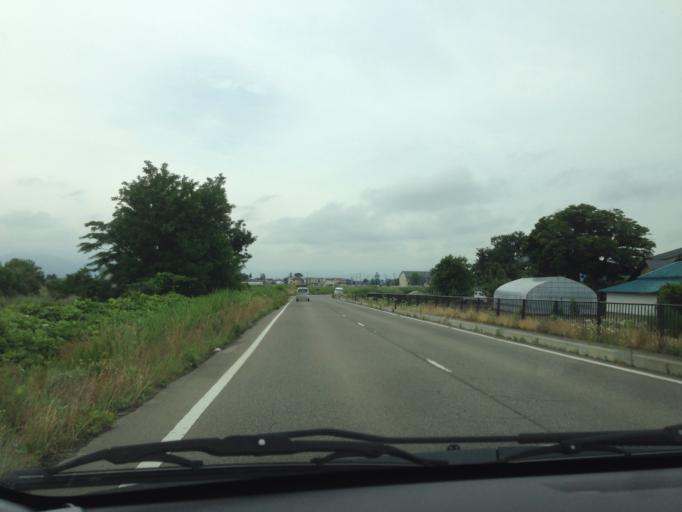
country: JP
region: Fukushima
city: Kitakata
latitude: 37.5708
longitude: 139.8891
